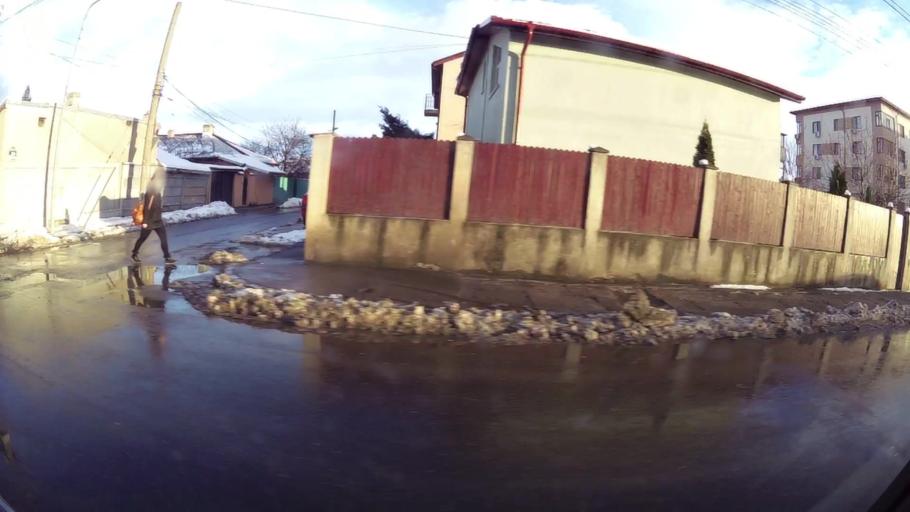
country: RO
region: Ilfov
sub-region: Comuna Popesti-Leordeni
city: Popesti-Leordeni
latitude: 44.3739
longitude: 26.1308
